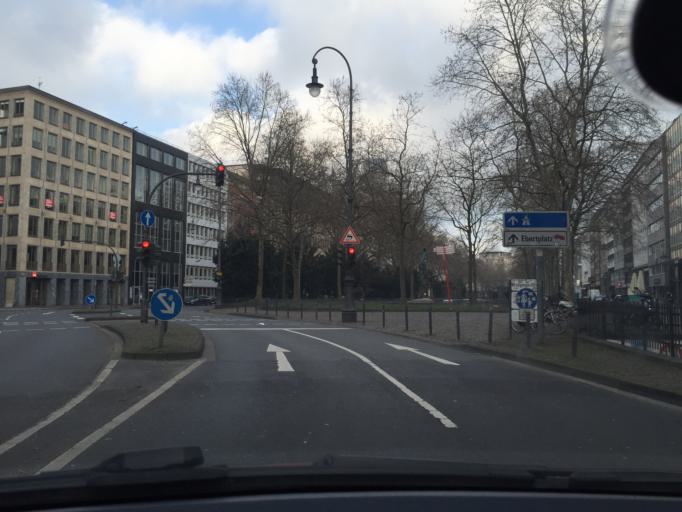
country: DE
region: North Rhine-Westphalia
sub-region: Regierungsbezirk Koln
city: Neustadt/Nord
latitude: 50.9425
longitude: 6.9404
